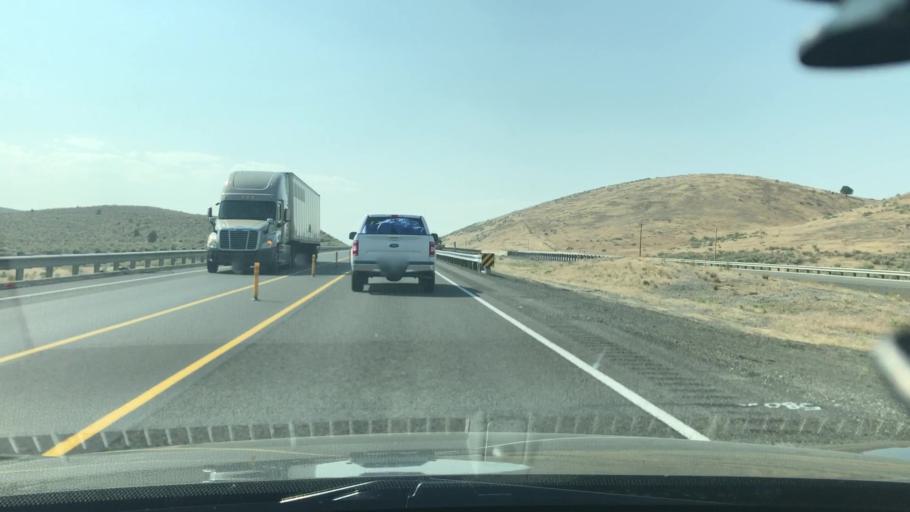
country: US
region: Oregon
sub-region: Baker County
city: Baker City
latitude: 44.6820
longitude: -117.6573
